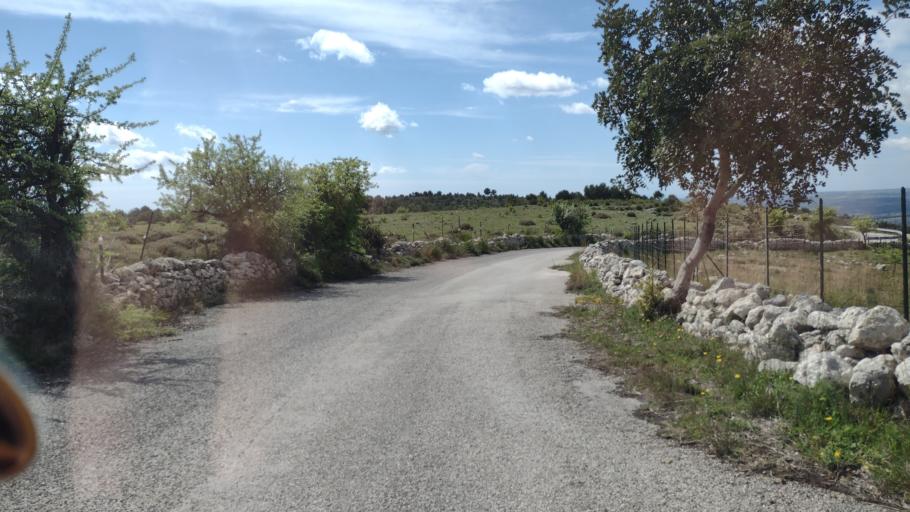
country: IT
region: Sicily
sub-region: Provincia di Siracusa
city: Noto
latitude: 36.9206
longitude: 14.9841
